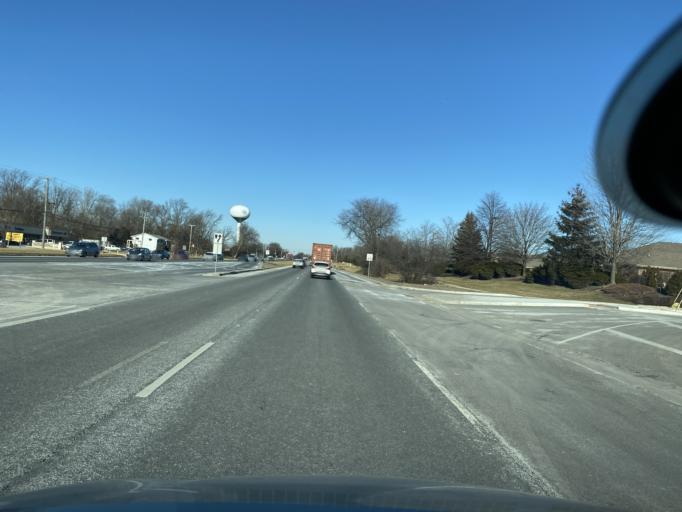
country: US
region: Illinois
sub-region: DuPage County
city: Willowbrook
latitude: 41.7632
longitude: -87.9448
